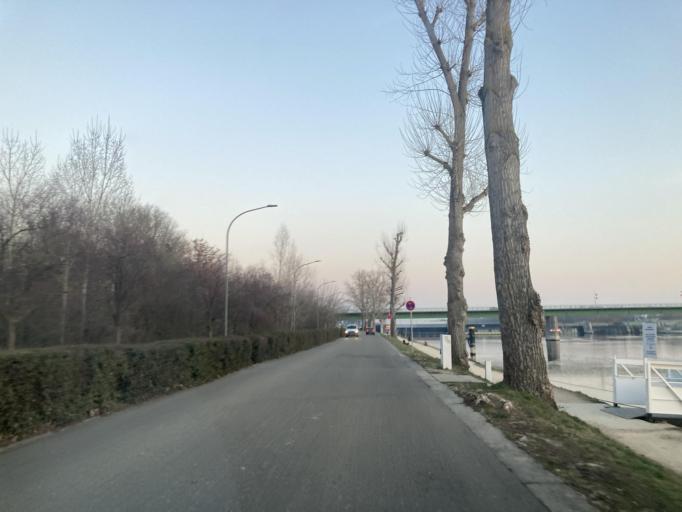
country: DE
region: Baden-Wuerttemberg
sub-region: Freiburg Region
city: Breisach am Rhein
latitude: 48.0249
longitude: 7.5807
